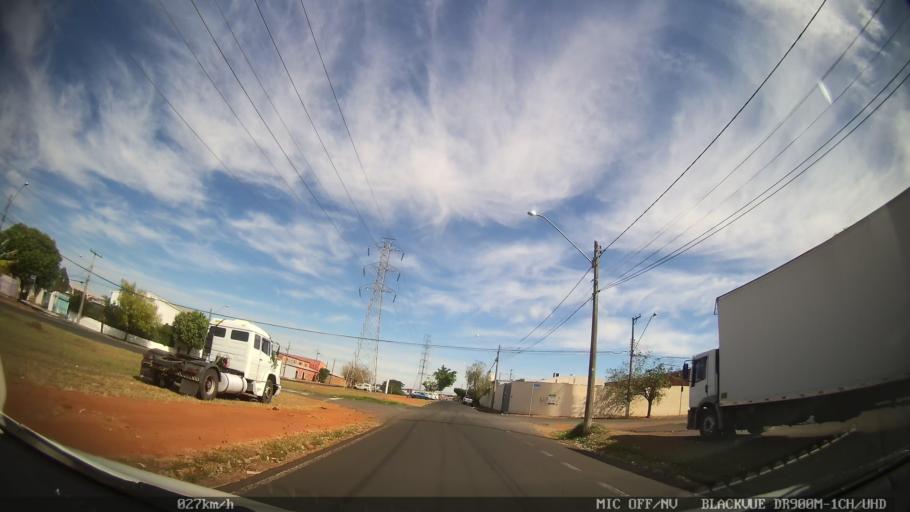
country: BR
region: Sao Paulo
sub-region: Sao Jose Do Rio Preto
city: Sao Jose do Rio Preto
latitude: -20.8362
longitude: -49.3538
